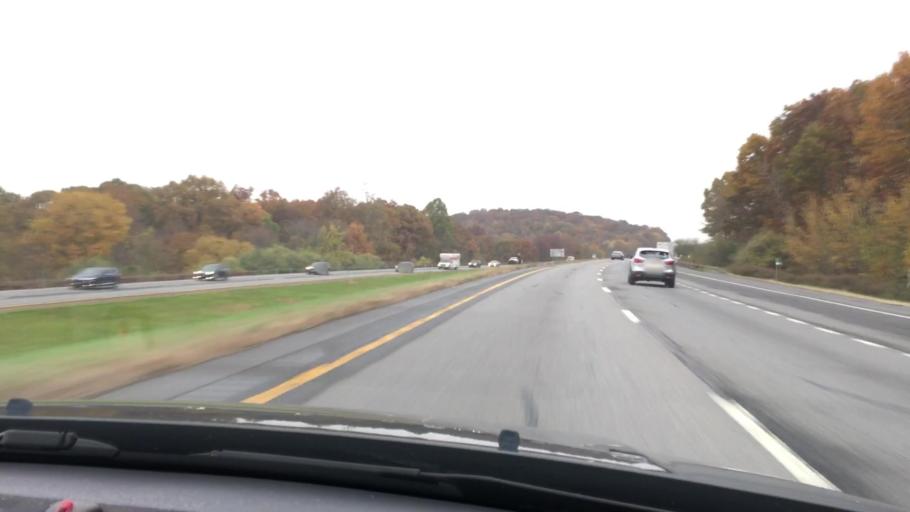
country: US
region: New York
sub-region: Putnam County
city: Brewster Hill
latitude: 41.4290
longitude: -73.6298
